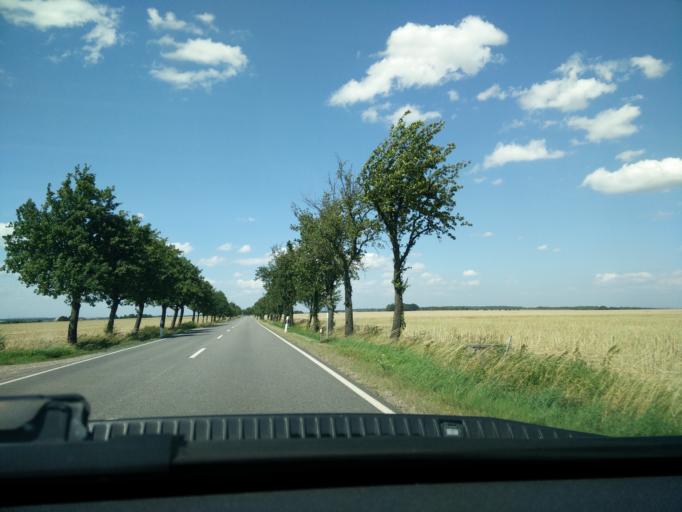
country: DE
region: Saxony
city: Narsdorf
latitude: 51.0335
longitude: 12.7227
